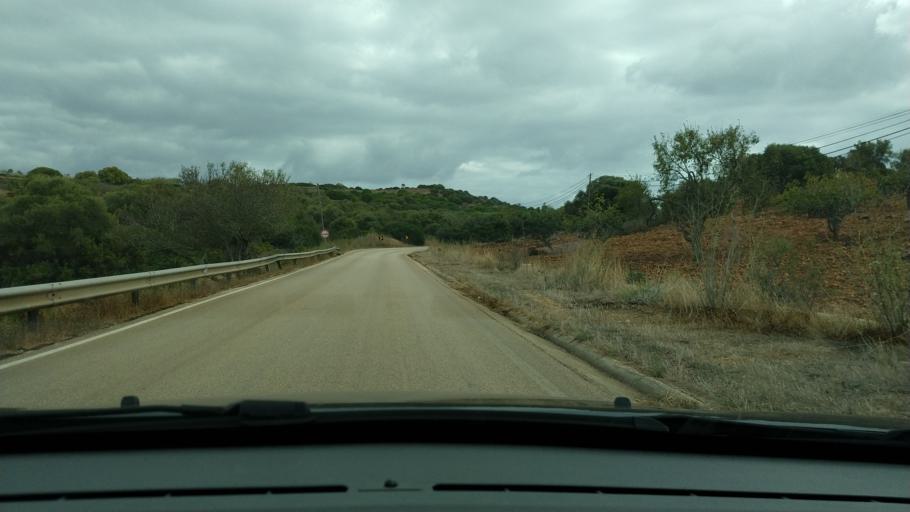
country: PT
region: Faro
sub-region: Lagos
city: Lagos
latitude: 37.0847
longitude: -8.7777
